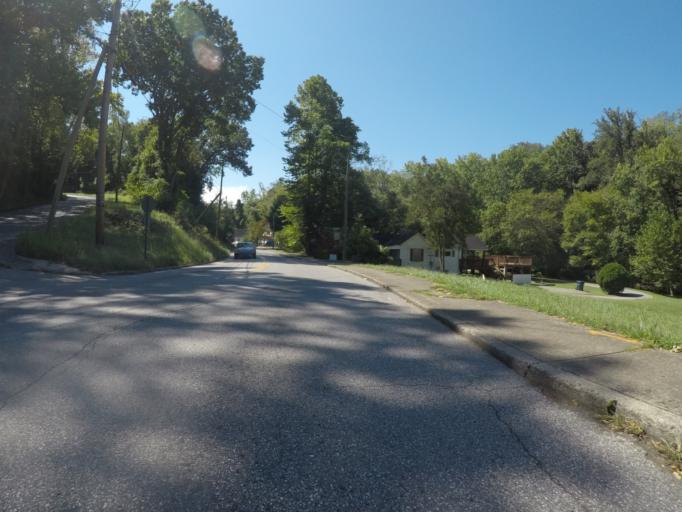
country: US
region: Kentucky
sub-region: Boyd County
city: Ashland
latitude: 38.4668
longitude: -82.6493
